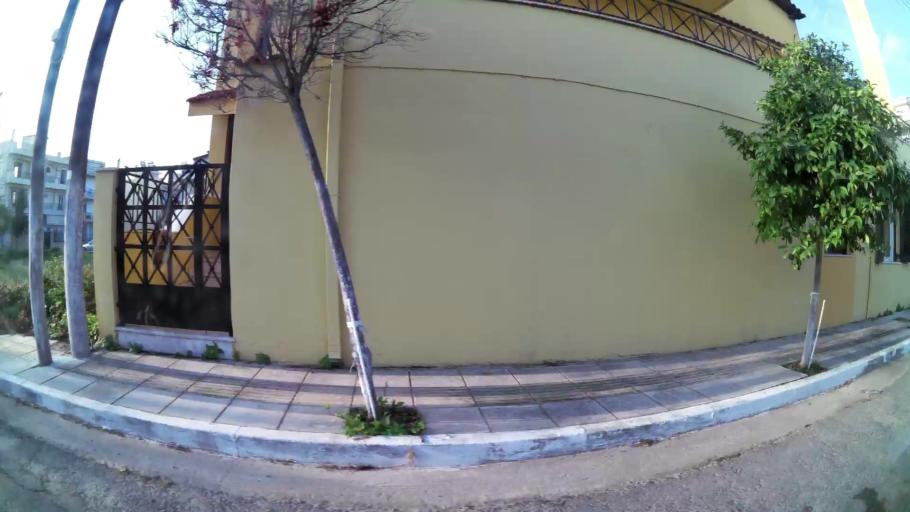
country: GR
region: Attica
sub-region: Nomarchia Dytikis Attikis
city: Zefyri
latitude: 38.0510
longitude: 23.7227
